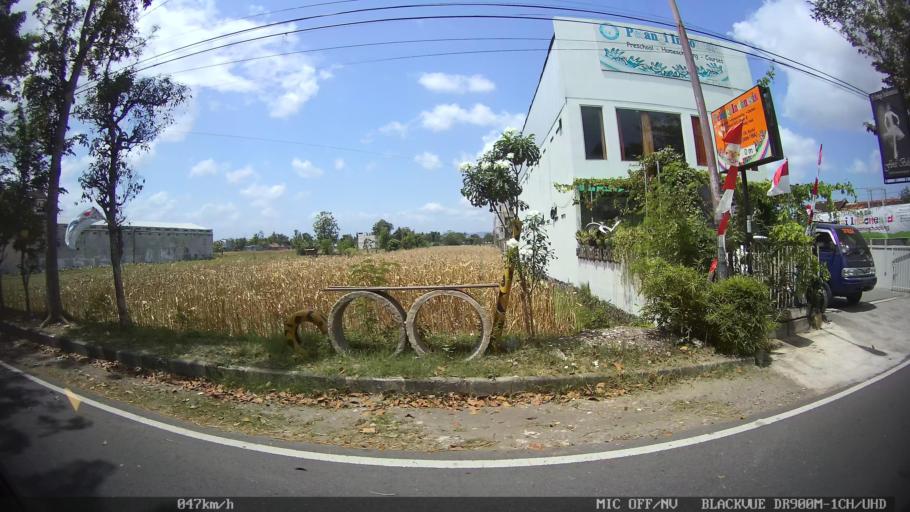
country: ID
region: Daerah Istimewa Yogyakarta
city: Bantul
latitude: -7.8831
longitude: 110.3358
